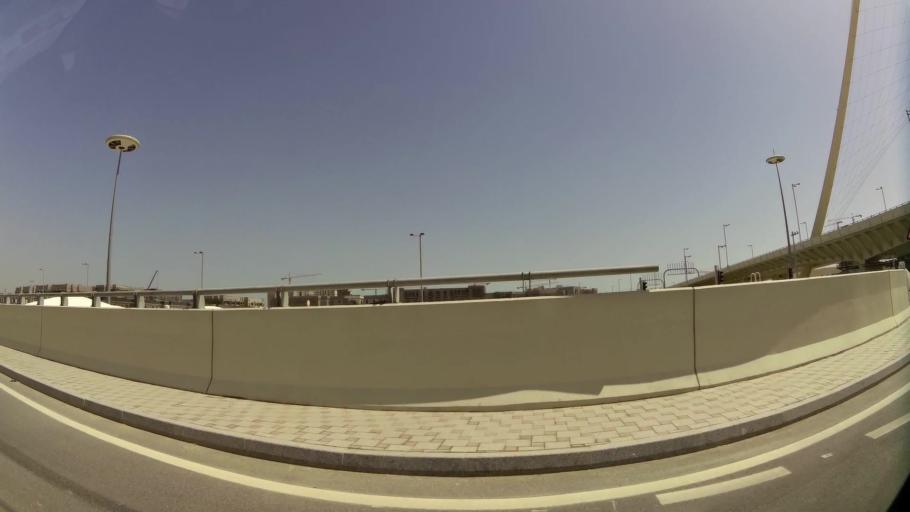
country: QA
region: Baladiyat Umm Salal
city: Umm Salal Muhammad
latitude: 25.4011
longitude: 51.5140
